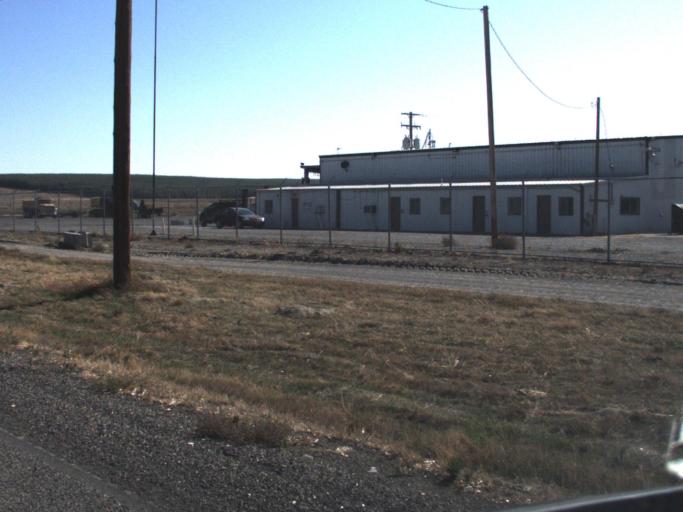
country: US
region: Washington
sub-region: Walla Walla County
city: Burbank
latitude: 46.2152
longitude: -118.8967
